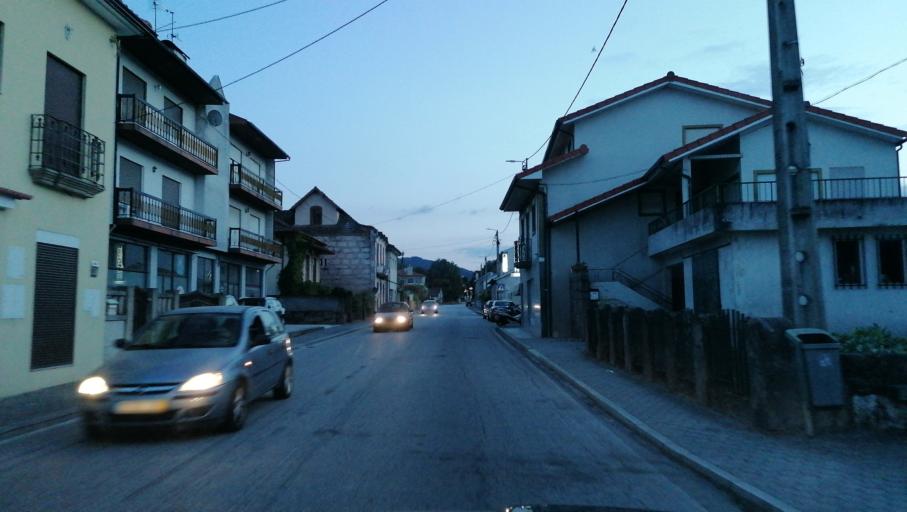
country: PT
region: Vila Real
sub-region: Vila Pouca de Aguiar
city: Vila Pouca de Aguiar
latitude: 41.5424
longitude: -7.6032
